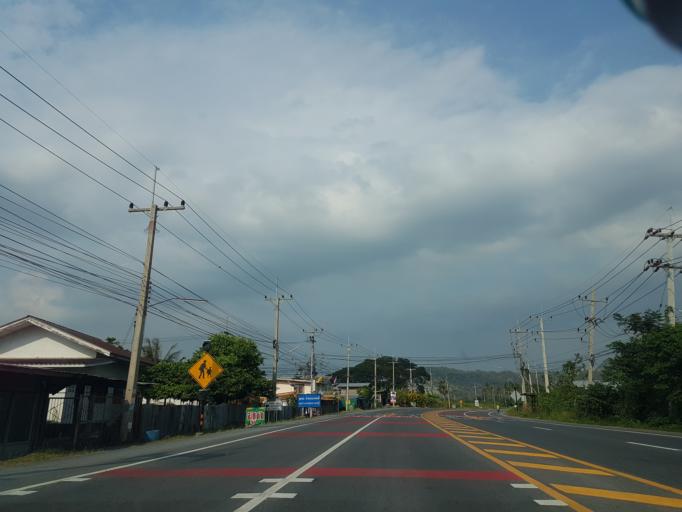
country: TH
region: Sara Buri
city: Phra Phutthabat
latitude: 14.6675
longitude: 100.7705
